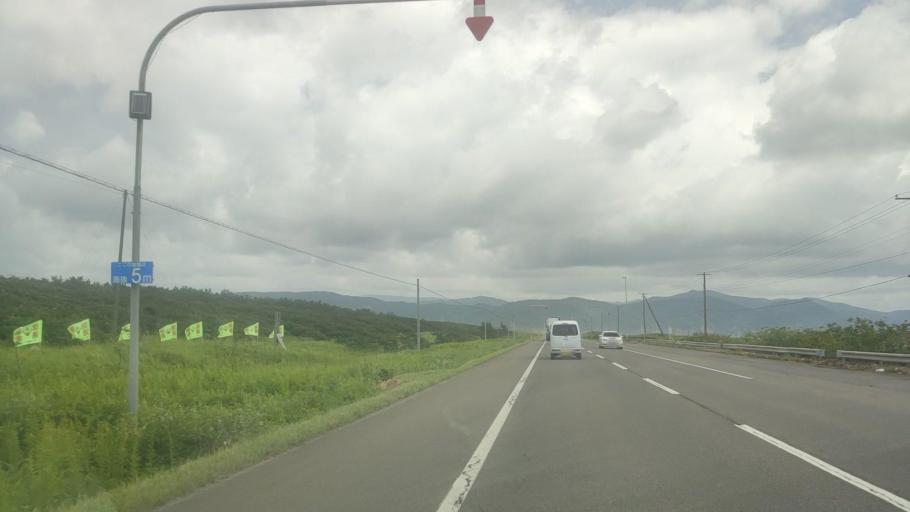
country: JP
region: Hokkaido
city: Niseko Town
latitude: 42.5610
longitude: 140.4313
